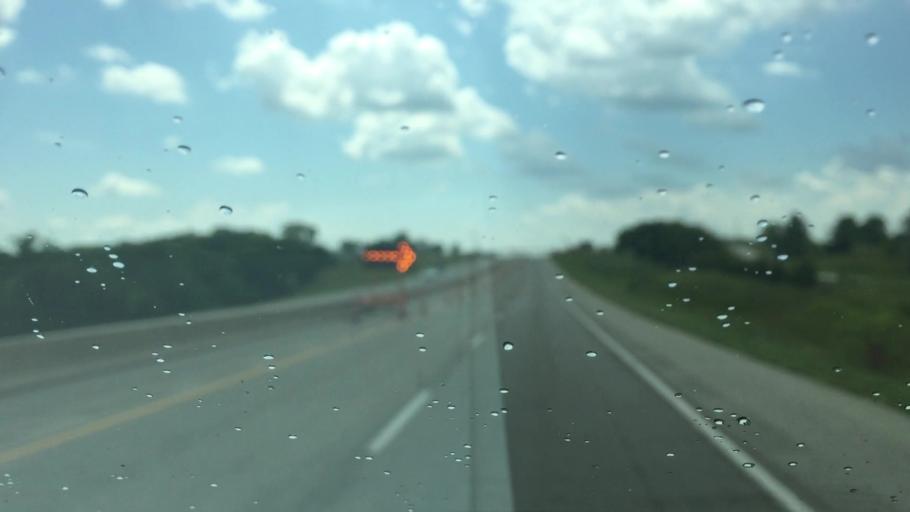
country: US
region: Kansas
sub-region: Shawnee County
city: Auburn
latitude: 38.9180
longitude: -95.7789
